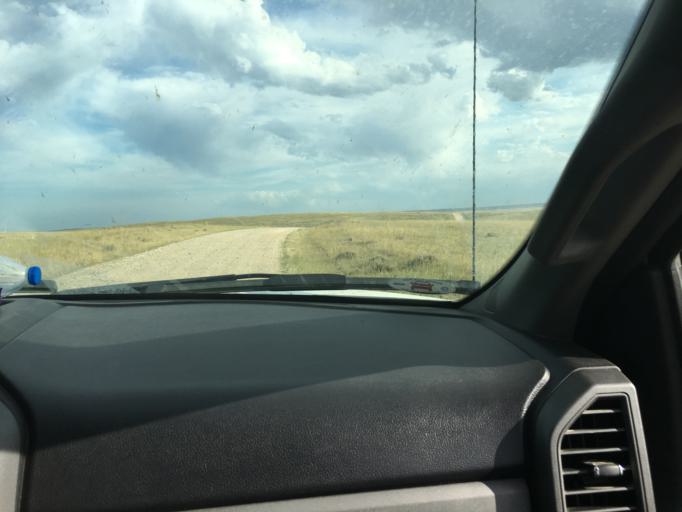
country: US
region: Wyoming
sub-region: Campbell County
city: Wright
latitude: 43.4966
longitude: -105.8599
